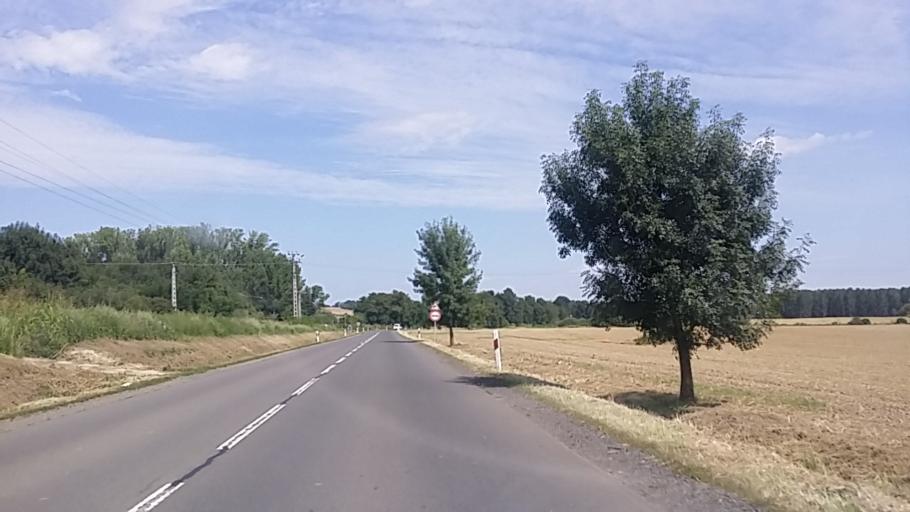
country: HU
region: Baranya
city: Sasd
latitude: 46.2692
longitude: 18.1039
